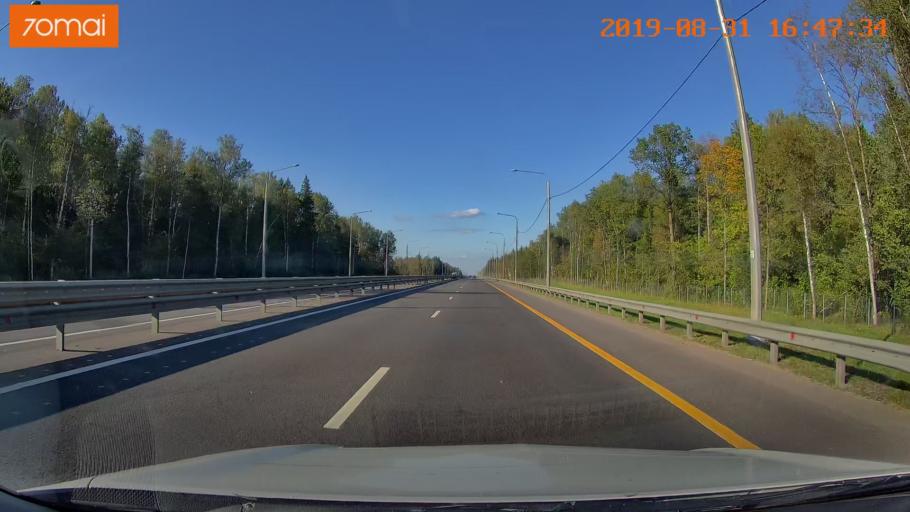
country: RU
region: Kaluga
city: Pyatovskiy
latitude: 54.6564
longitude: 36.1399
